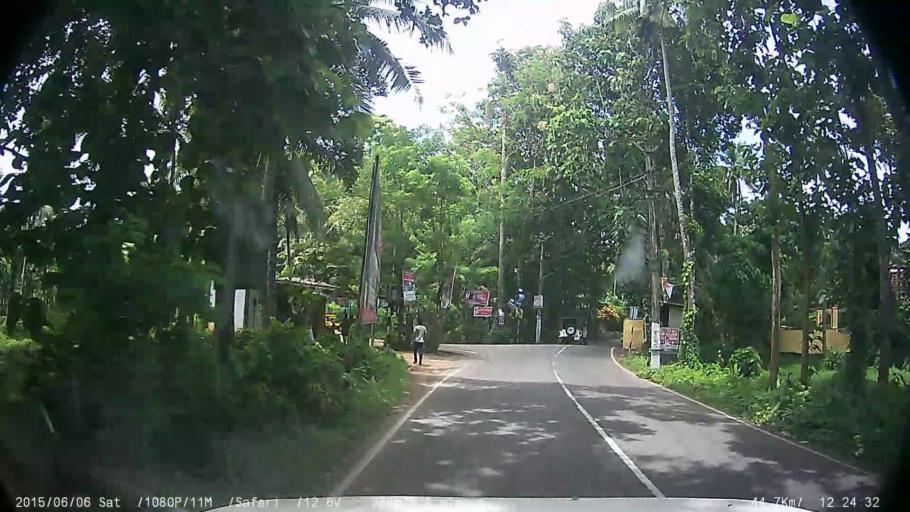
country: IN
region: Kerala
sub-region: Kottayam
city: Palackattumala
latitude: 9.6575
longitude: 76.6125
